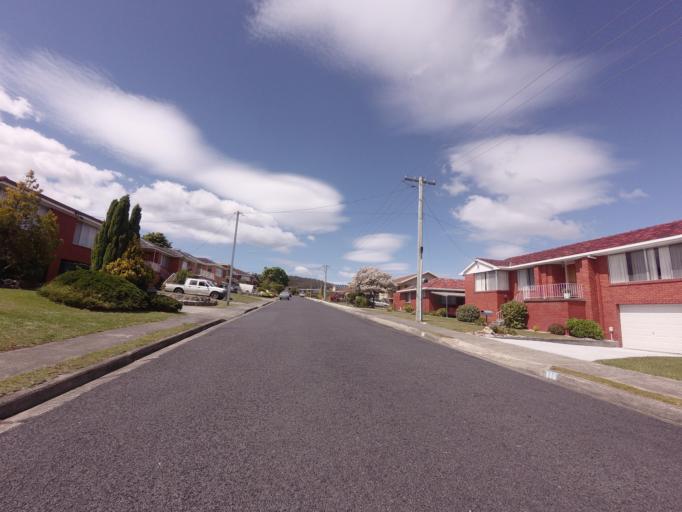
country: AU
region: Tasmania
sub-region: Clarence
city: Howrah
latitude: -42.8784
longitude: 147.4028
